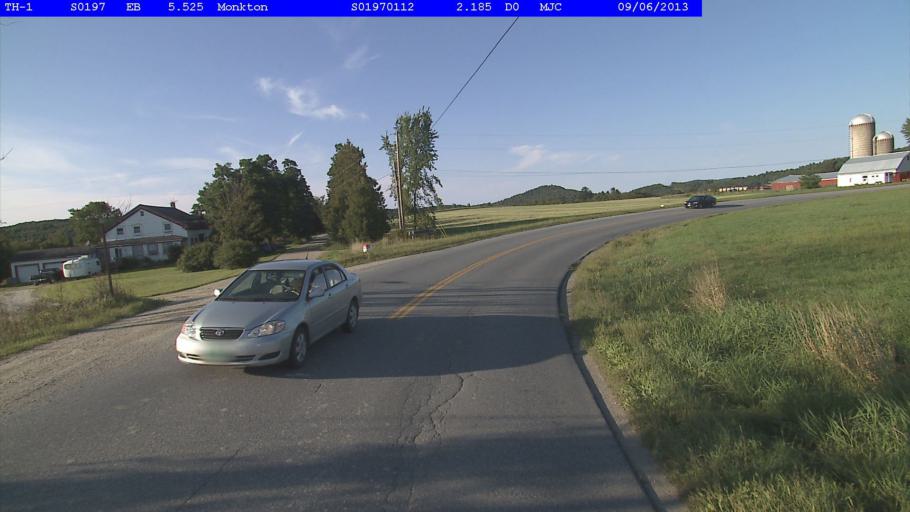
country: US
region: Vermont
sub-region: Addison County
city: Vergennes
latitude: 44.2139
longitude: -73.1641
